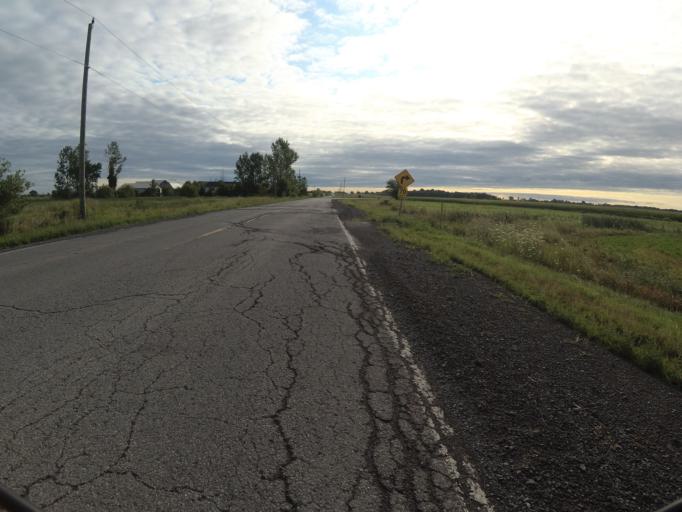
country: CA
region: Ontario
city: Clarence-Rockland
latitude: 45.3174
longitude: -75.4084
